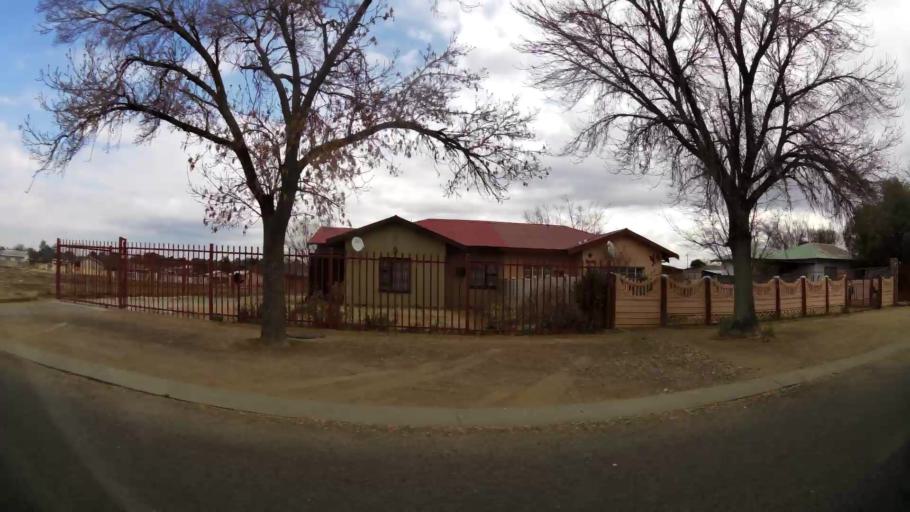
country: ZA
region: Orange Free State
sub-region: Fezile Dabi District Municipality
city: Kroonstad
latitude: -27.6419
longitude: 27.2291
